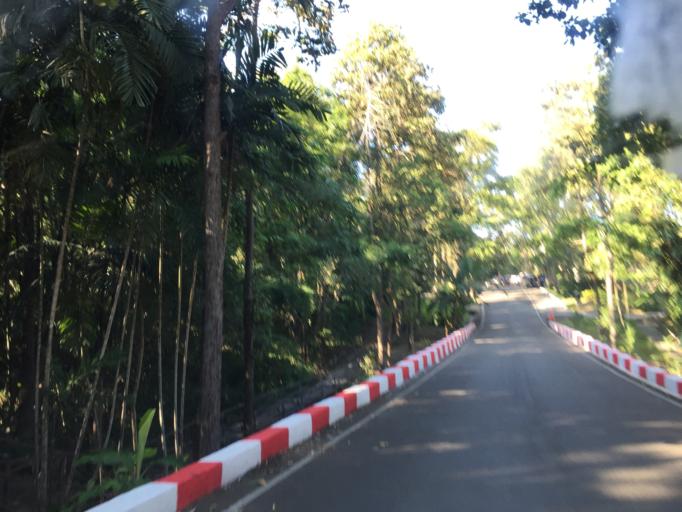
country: TH
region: Chiang Mai
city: Chiang Mai
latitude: 18.8048
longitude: 98.9430
